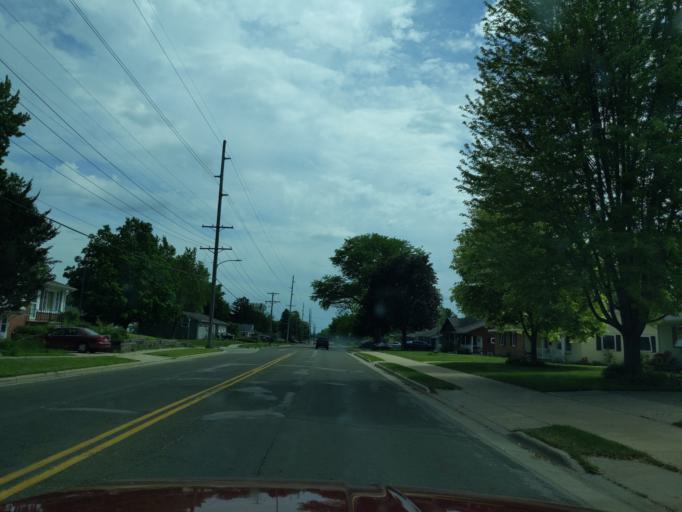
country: US
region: Wisconsin
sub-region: Dane County
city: Sun Prairie
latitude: 43.1863
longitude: -89.2264
